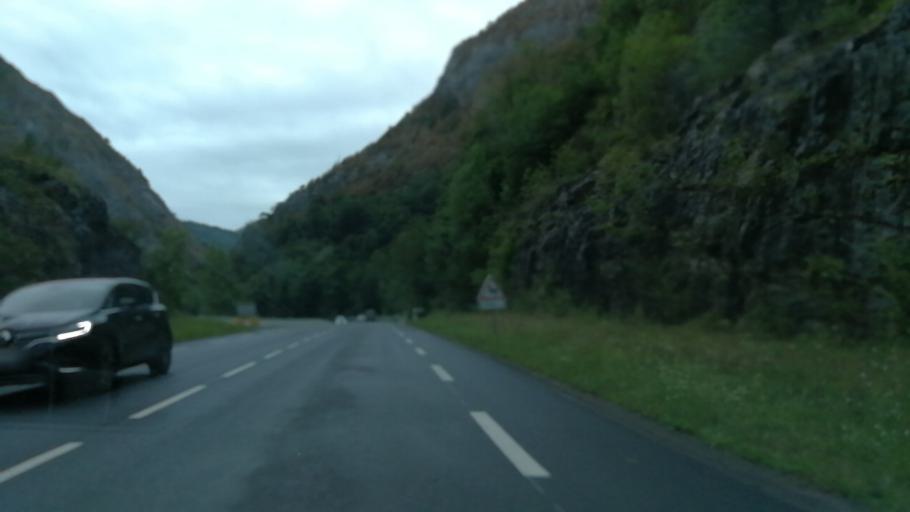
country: FR
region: Aquitaine
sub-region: Departement des Pyrenees-Atlantiques
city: Arette
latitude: 43.0662
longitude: -0.6018
